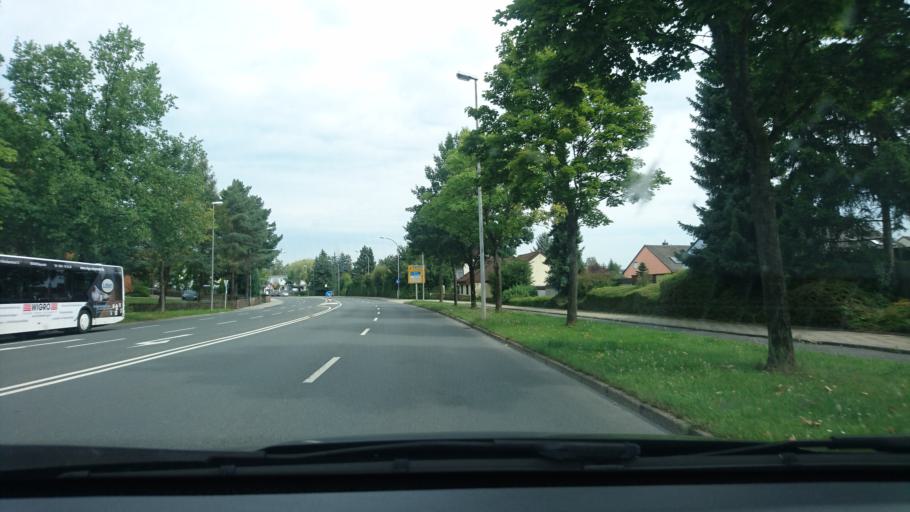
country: DE
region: Bavaria
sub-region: Upper Franconia
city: Heinersreuth
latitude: 49.9443
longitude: 11.5461
